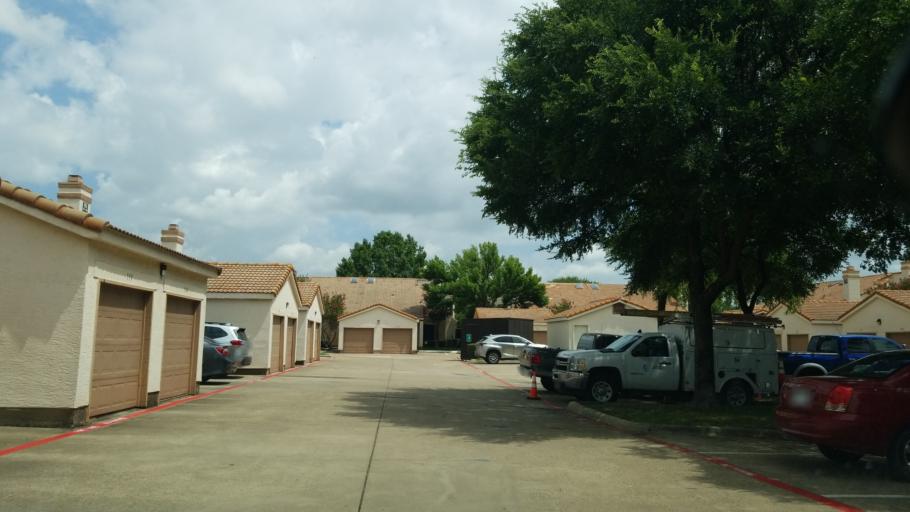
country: US
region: Texas
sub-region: Dallas County
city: Farmers Branch
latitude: 32.9291
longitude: -96.9530
